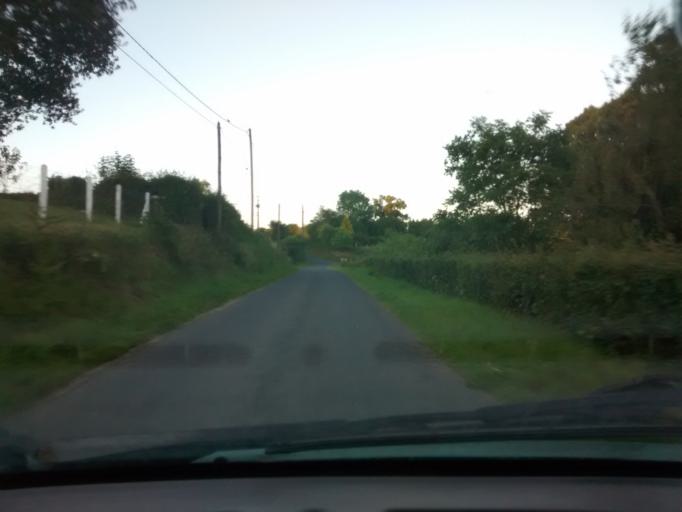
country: FR
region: Lower Normandy
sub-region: Departement de la Manche
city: Saint-Jean-des-Baisants
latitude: 49.1405
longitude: -1.0231
